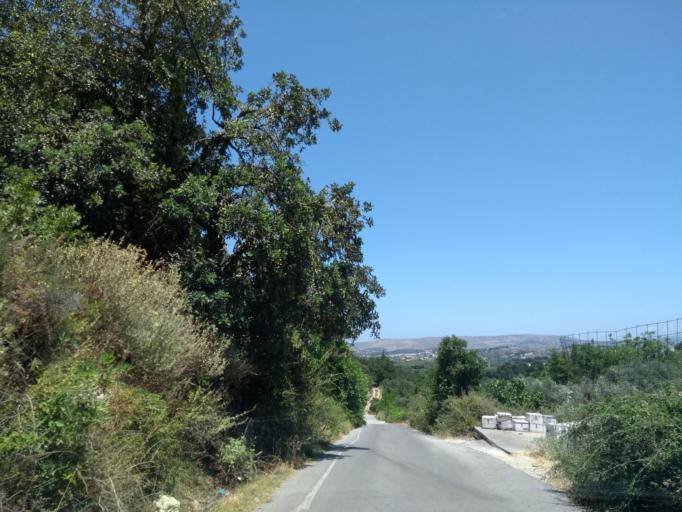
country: GR
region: Crete
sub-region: Nomos Chanias
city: Georgioupolis
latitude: 35.3166
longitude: 24.3019
